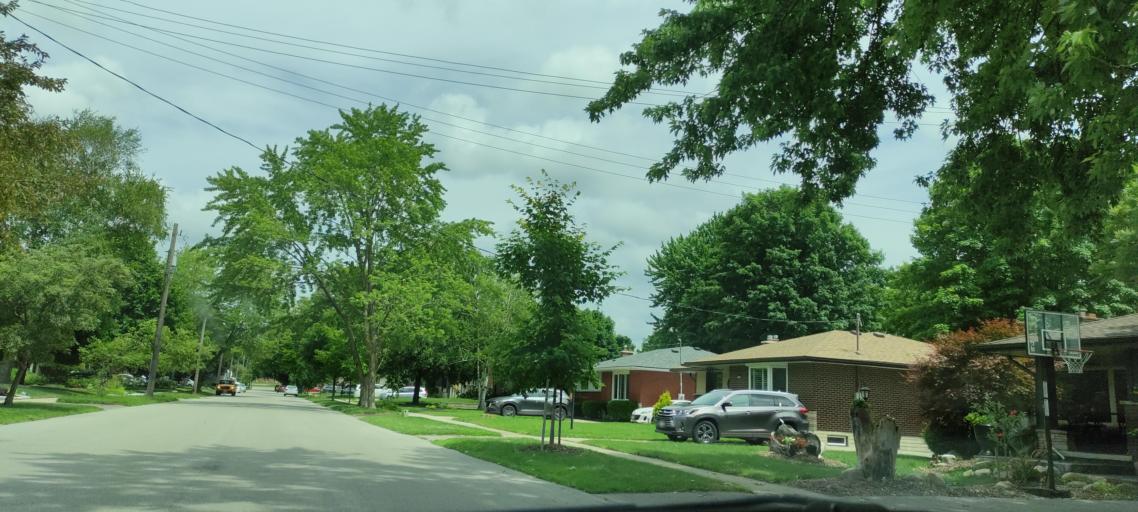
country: CA
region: Ontario
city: Kitchener
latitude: 43.4415
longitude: -80.4520
